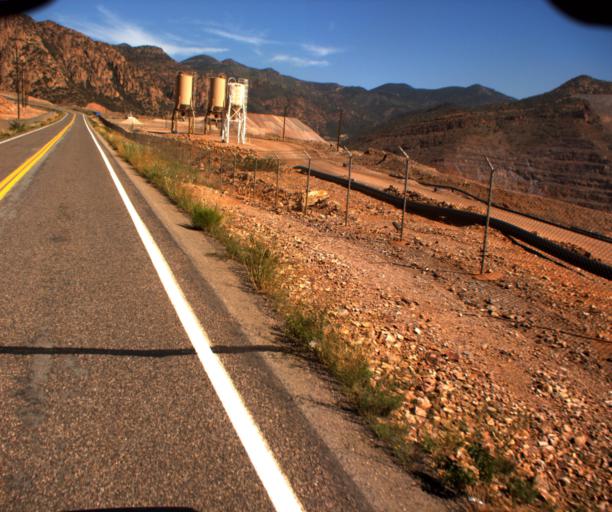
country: US
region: Arizona
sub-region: Greenlee County
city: Morenci
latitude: 33.1246
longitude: -109.3676
